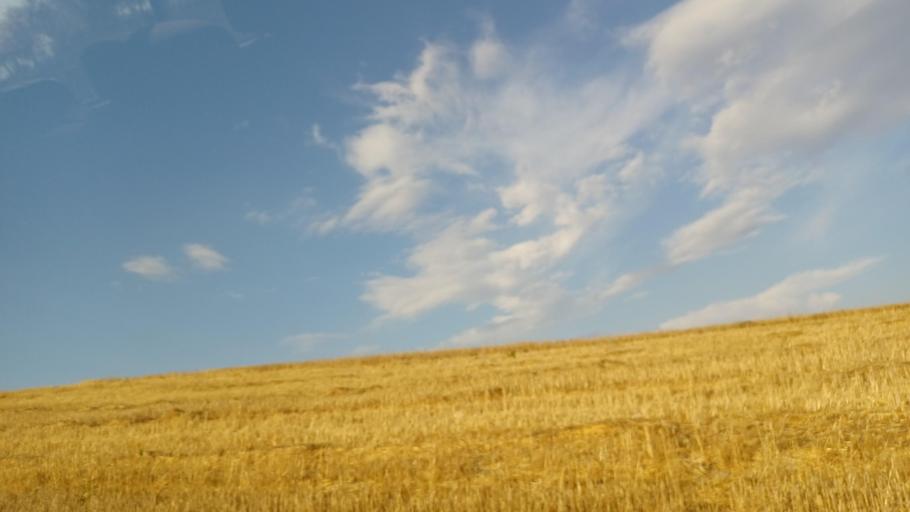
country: CY
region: Pafos
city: Tala
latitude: 34.9033
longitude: 32.4997
